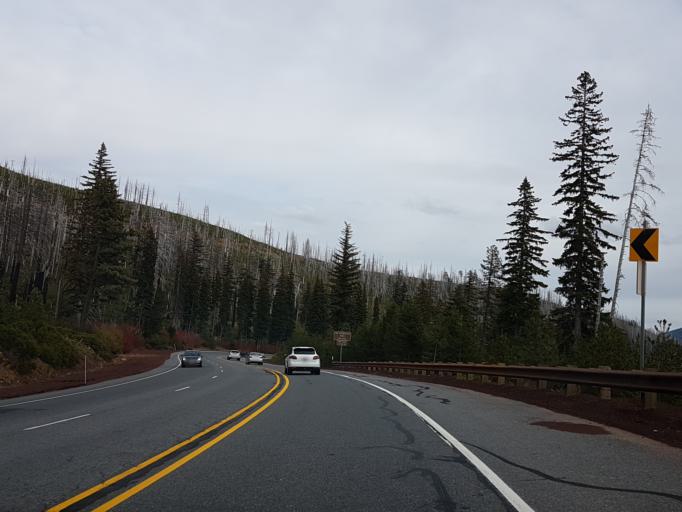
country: US
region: Oregon
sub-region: Deschutes County
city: Sisters
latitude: 44.4230
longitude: -121.8037
